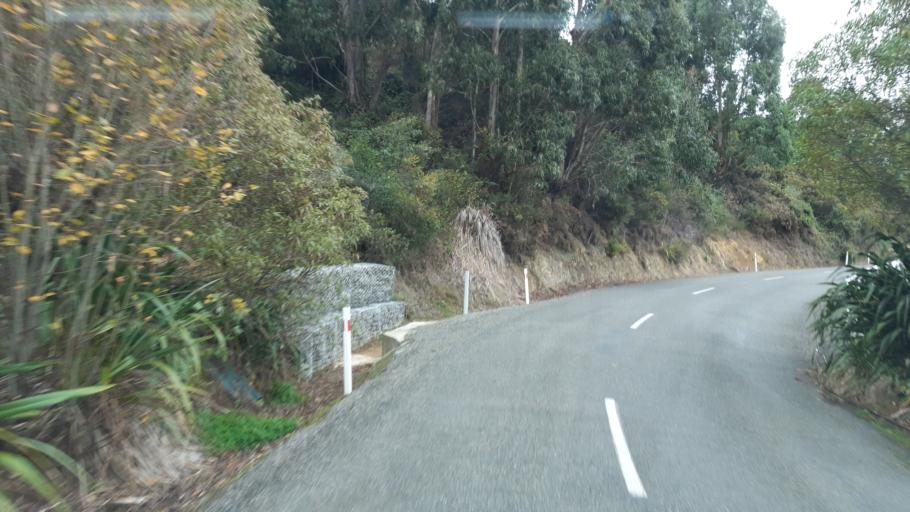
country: NZ
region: Nelson
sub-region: Nelson City
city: Nelson
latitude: -41.1680
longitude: 173.4208
